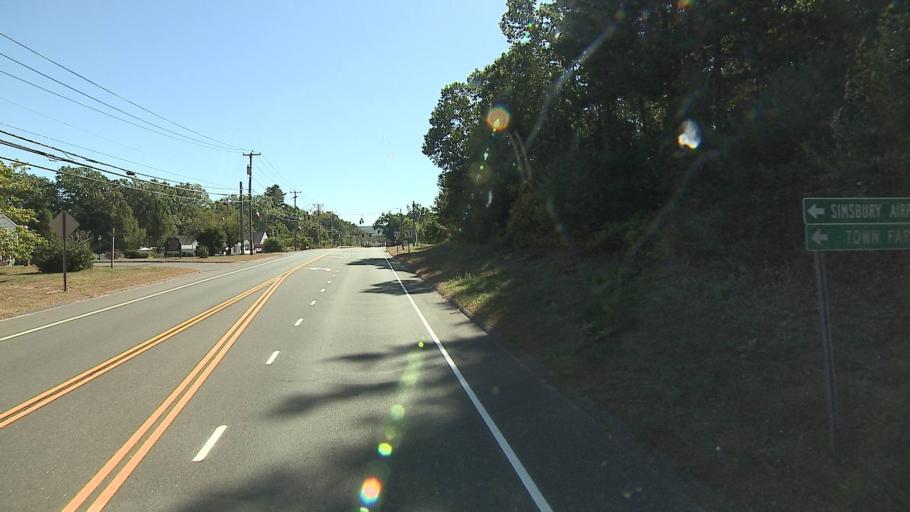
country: US
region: Connecticut
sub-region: Hartford County
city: Tariffville
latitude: 41.9094
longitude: -72.7885
